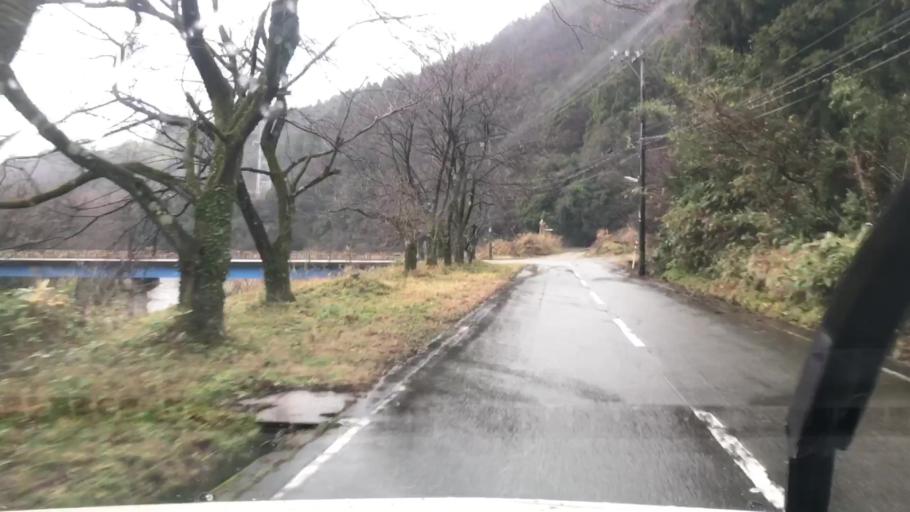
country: JP
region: Toyama
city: Kamiichi
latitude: 36.5984
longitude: 137.3047
